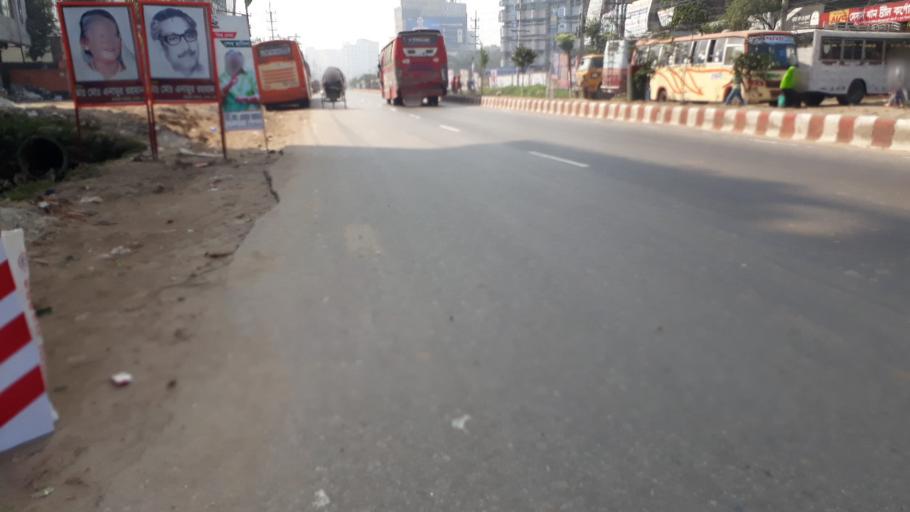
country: BD
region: Dhaka
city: Tungi
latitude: 23.8579
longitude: 90.2621
